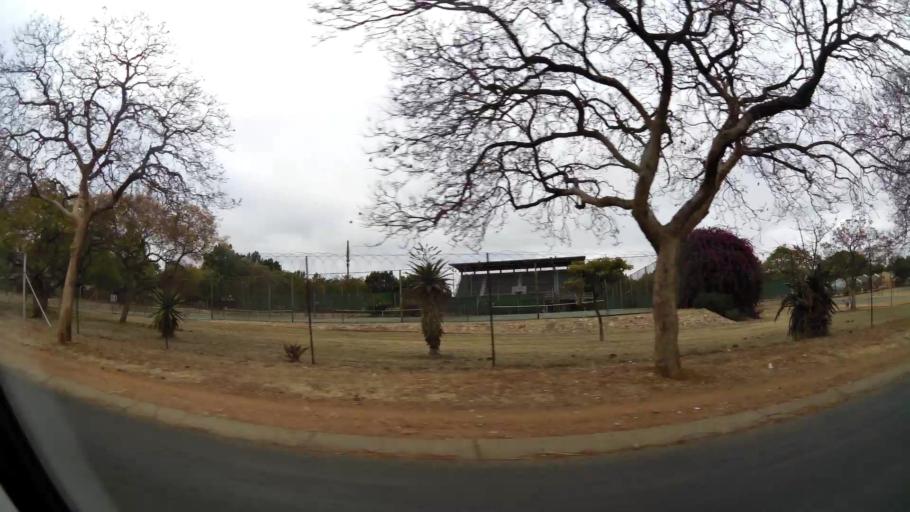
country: ZA
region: Limpopo
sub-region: Capricorn District Municipality
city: Polokwane
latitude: -23.9007
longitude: 29.4606
